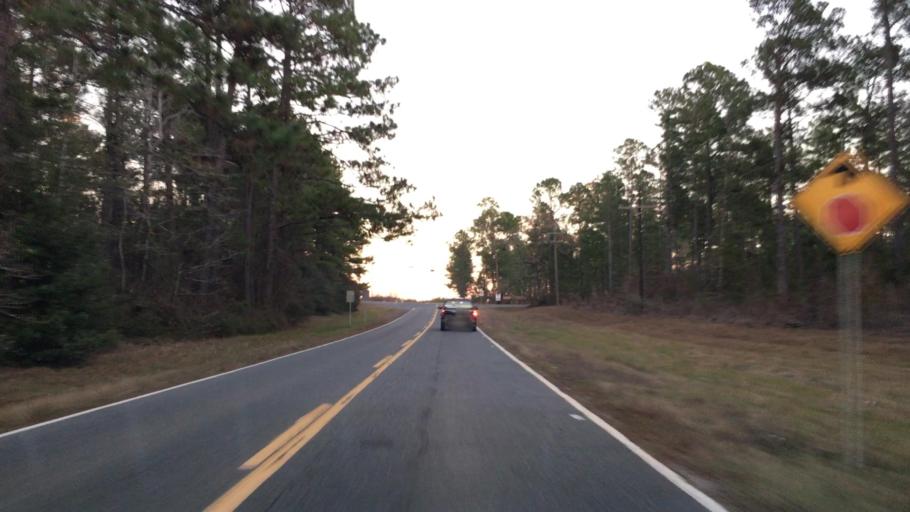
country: US
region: Louisiana
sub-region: Vernon Parish
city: Fort Polk South
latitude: 31.0290
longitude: -93.1918
